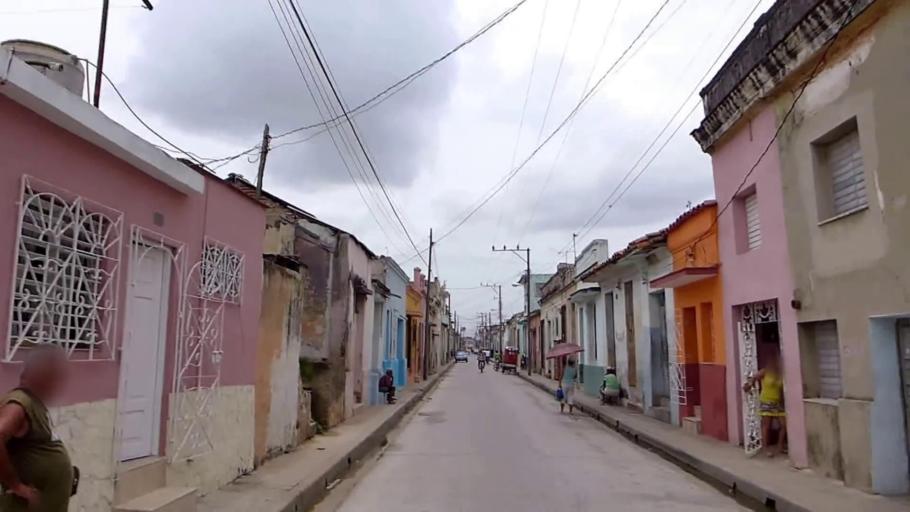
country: CU
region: Camaguey
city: Camaguey
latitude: 21.3808
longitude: -77.9261
